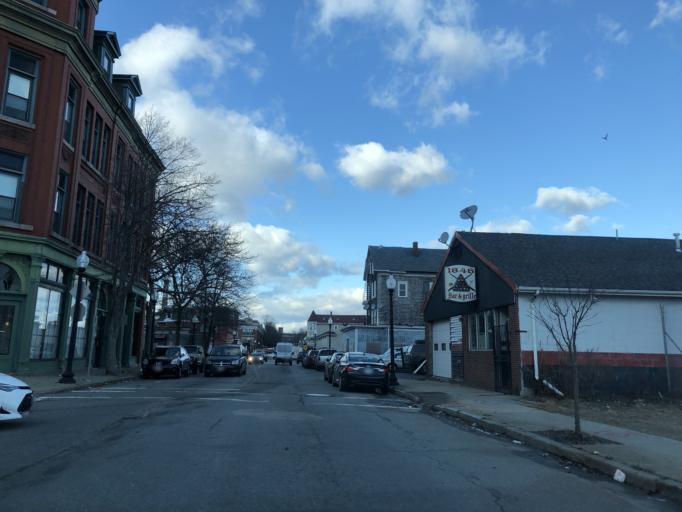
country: US
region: Massachusetts
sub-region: Bristol County
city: New Bedford
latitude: 41.6500
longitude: -70.9289
